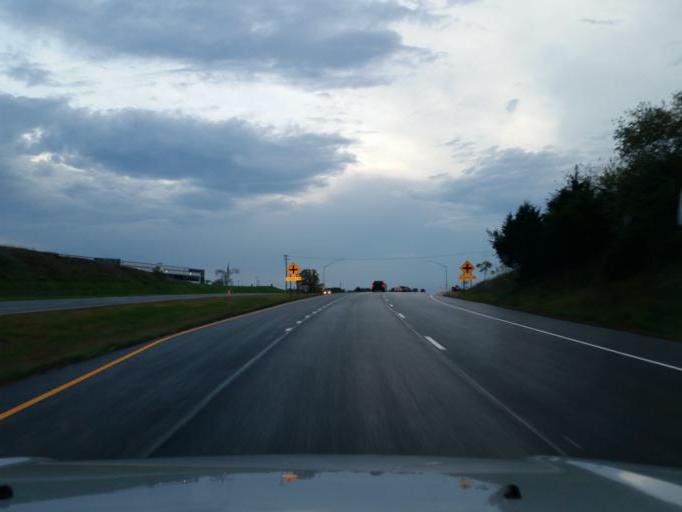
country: US
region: Maryland
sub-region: Frederick County
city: Emmitsburg
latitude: 39.6987
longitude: -77.3160
